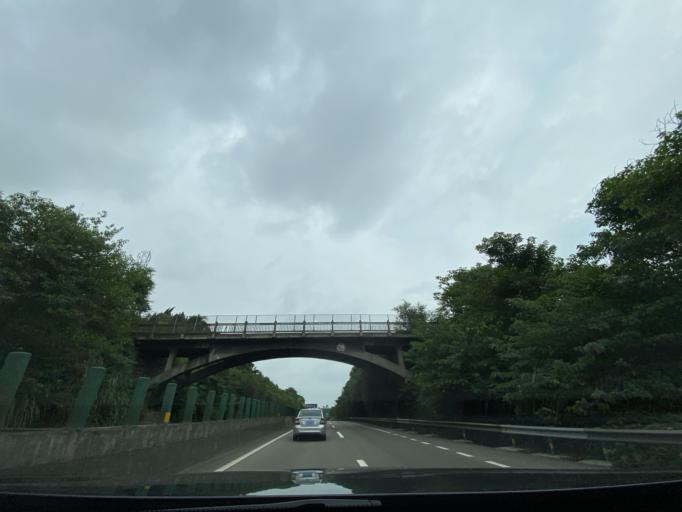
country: CN
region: Sichuan
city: Neijiang
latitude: 29.6643
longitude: 104.9788
